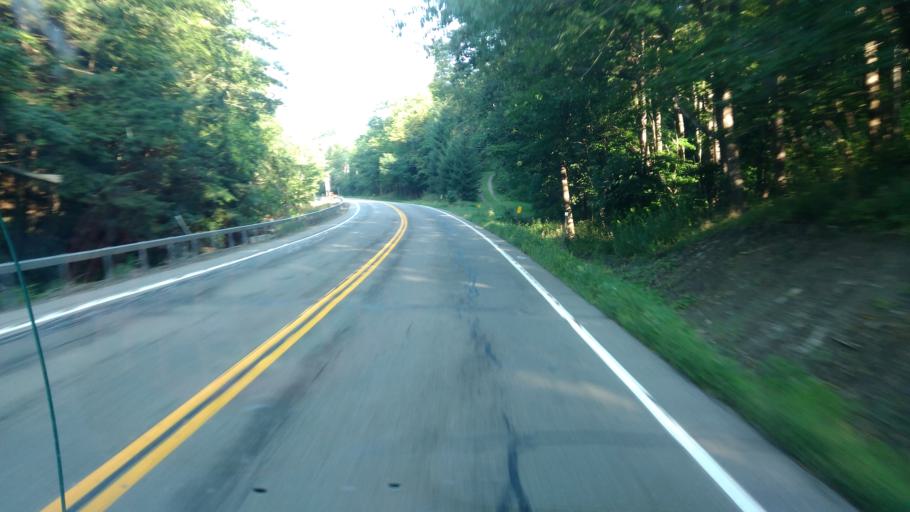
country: US
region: New York
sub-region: Allegany County
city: Andover
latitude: 42.1397
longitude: -77.6636
